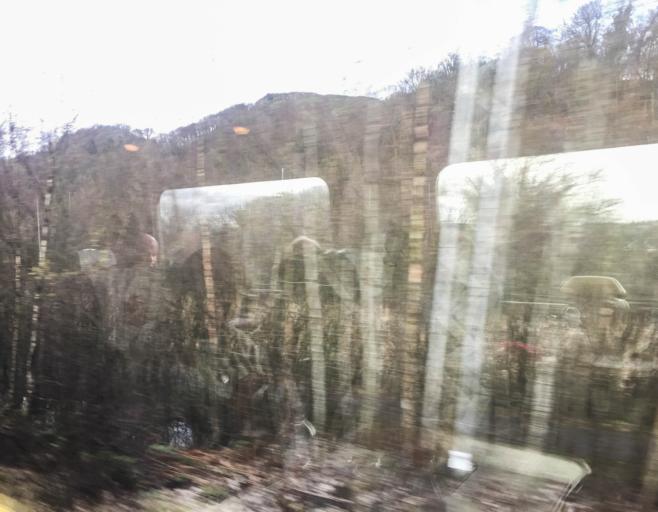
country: GB
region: Scotland
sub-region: Renfrewshire
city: Bishopton
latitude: 55.9322
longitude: -4.5074
